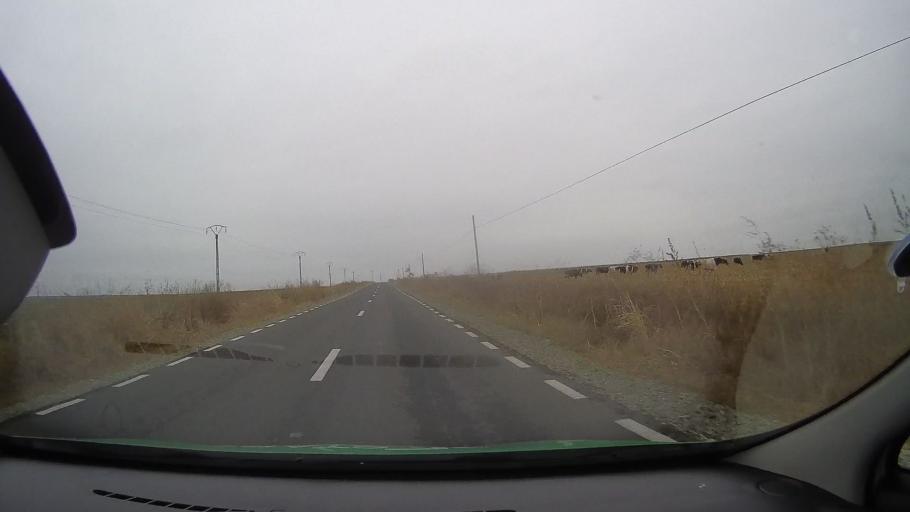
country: RO
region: Constanta
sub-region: Comuna Tortoman
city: Tortoman
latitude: 44.3539
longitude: 28.2141
